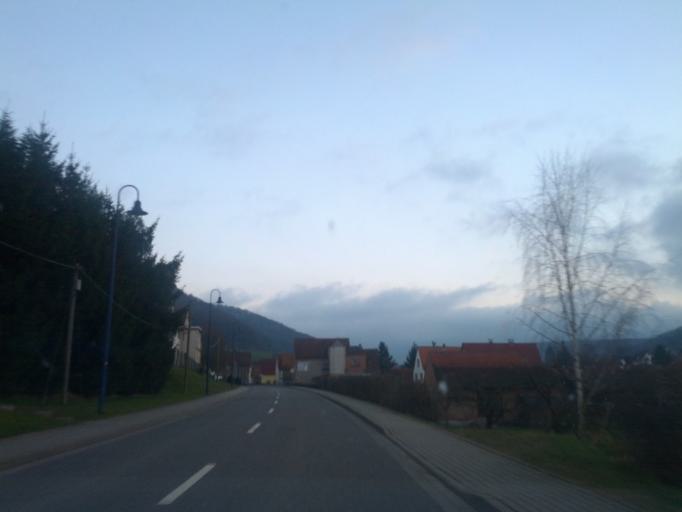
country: DE
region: Thuringia
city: Treffurt
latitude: 51.1085
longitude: 10.2212
